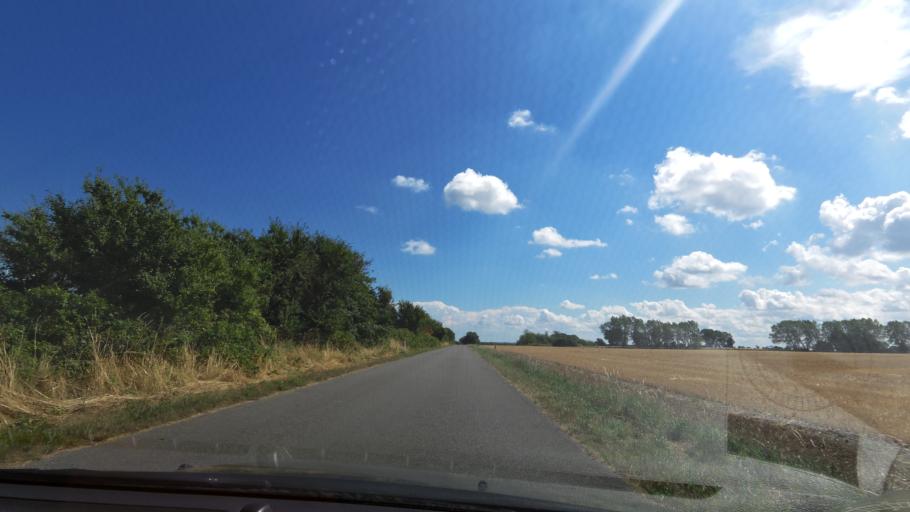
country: DK
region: South Denmark
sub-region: Nordfyns Kommune
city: Otterup
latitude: 55.5491
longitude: 10.4855
